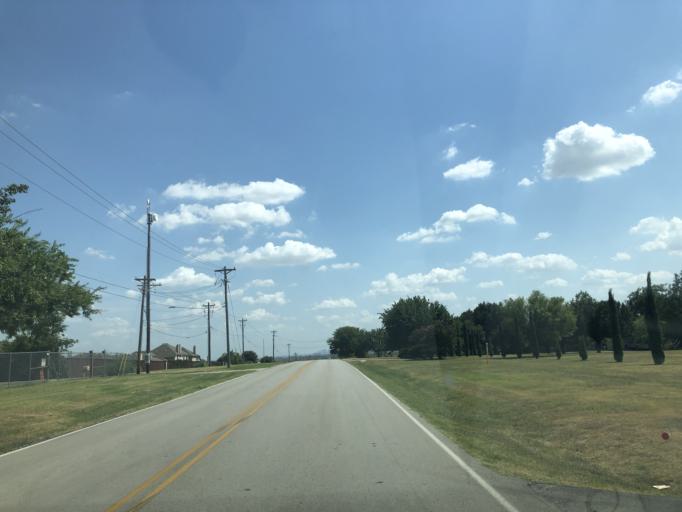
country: US
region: Texas
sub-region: Tarrant County
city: Haslet
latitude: 32.9266
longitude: -97.3315
